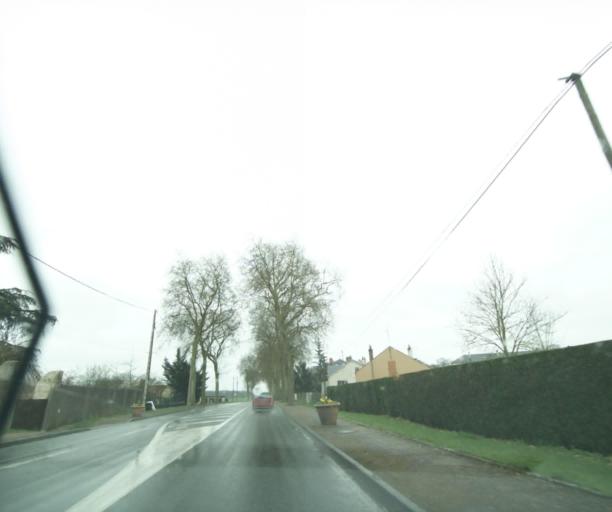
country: FR
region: Centre
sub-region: Departement du Loiret
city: Chevilly
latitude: 48.0224
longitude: 1.8752
